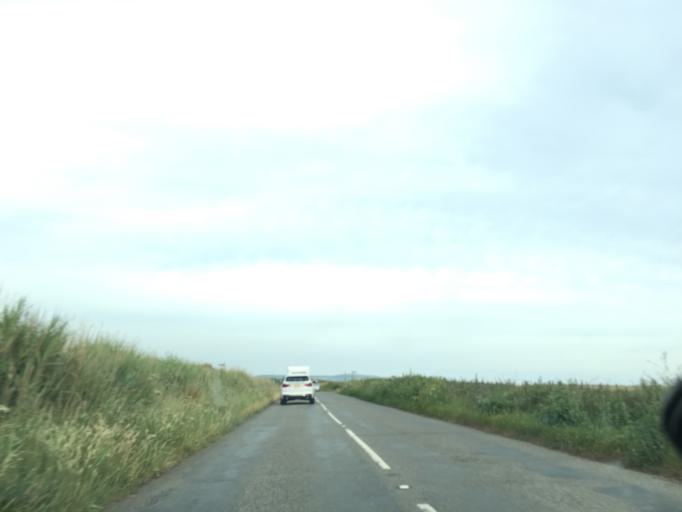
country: GB
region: England
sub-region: Isle of Wight
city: Shalfleet
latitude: 50.6430
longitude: -1.4358
